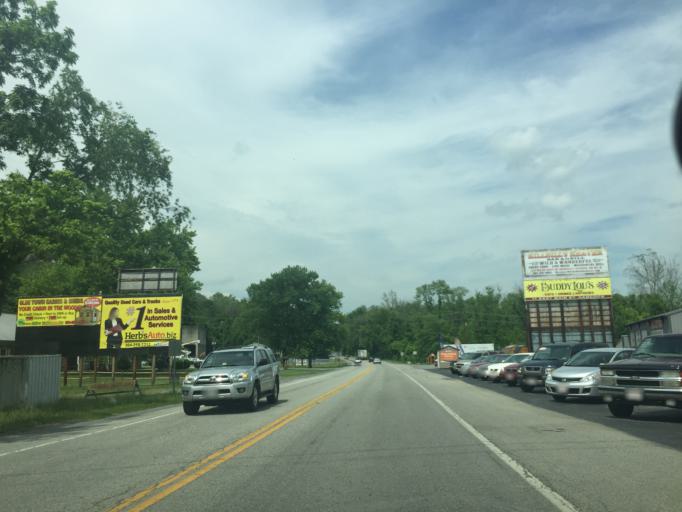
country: US
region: West Virginia
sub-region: Morgan County
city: Berkeley Springs
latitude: 39.6330
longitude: -78.2234
